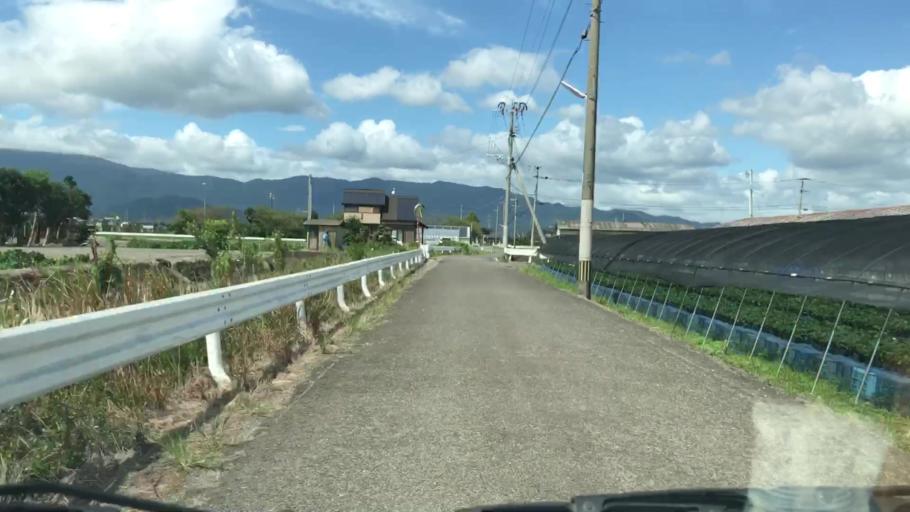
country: JP
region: Saga Prefecture
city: Saga-shi
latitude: 33.2362
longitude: 130.2120
